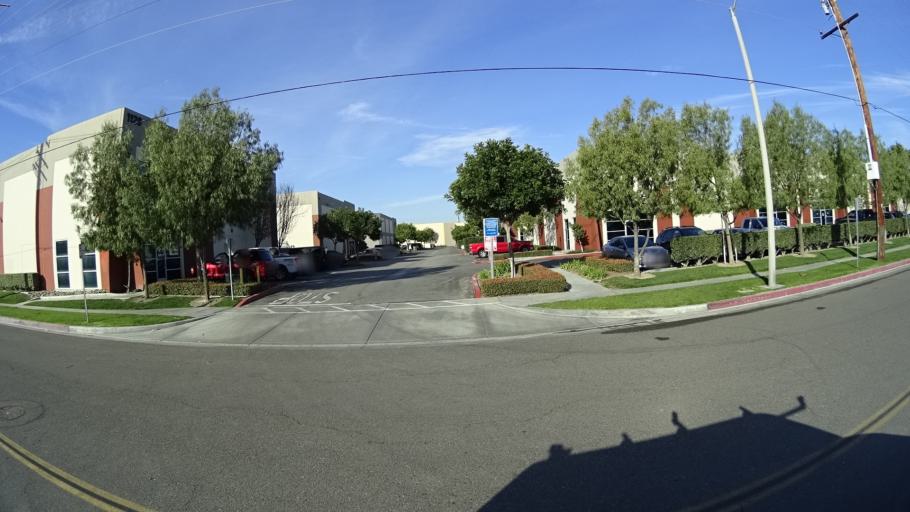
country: US
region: California
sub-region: Orange County
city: Anaheim
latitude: 33.8501
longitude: -117.9154
